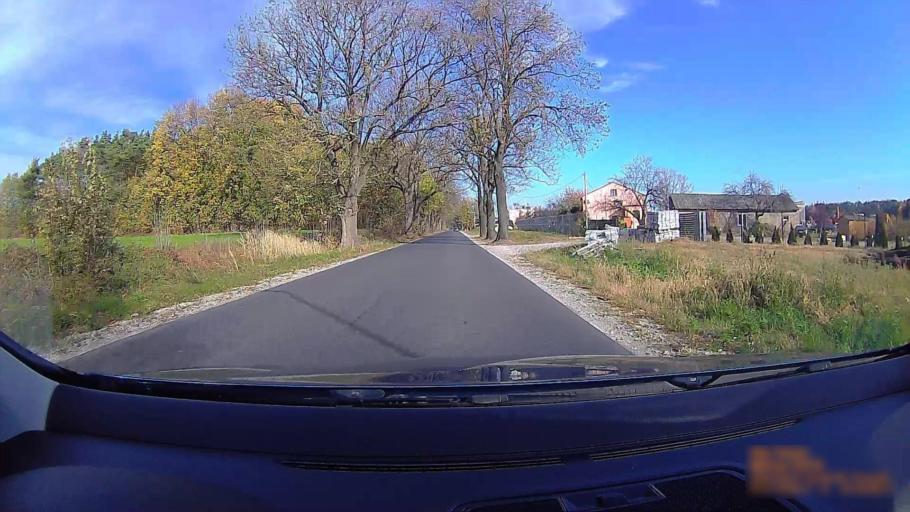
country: PL
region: Greater Poland Voivodeship
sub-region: Powiat ostrzeszowski
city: Doruchow
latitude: 51.3947
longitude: 18.0580
